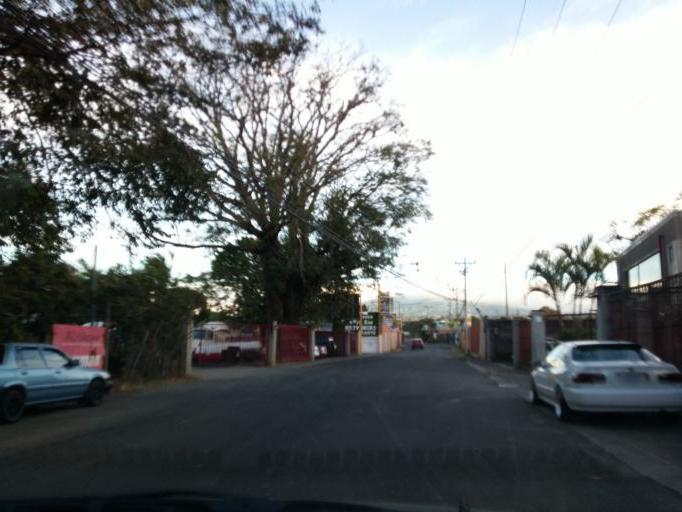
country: CR
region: Alajuela
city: Alajuela
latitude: 9.9996
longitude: -84.2249
